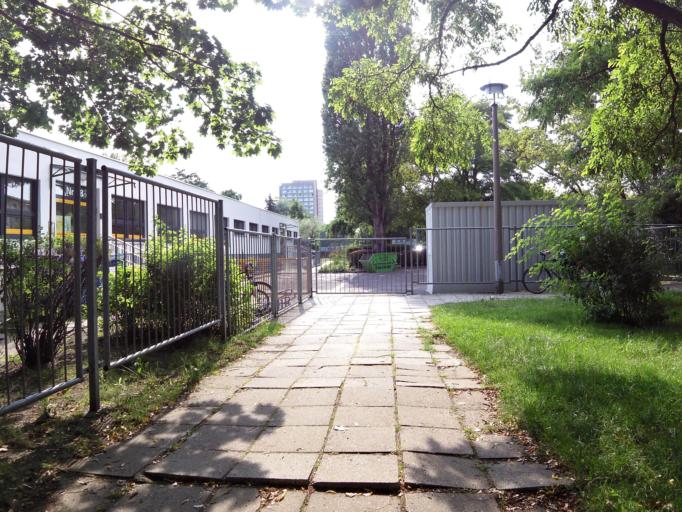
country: DE
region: Saxony
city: Leipzig
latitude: 51.3553
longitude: 12.4294
